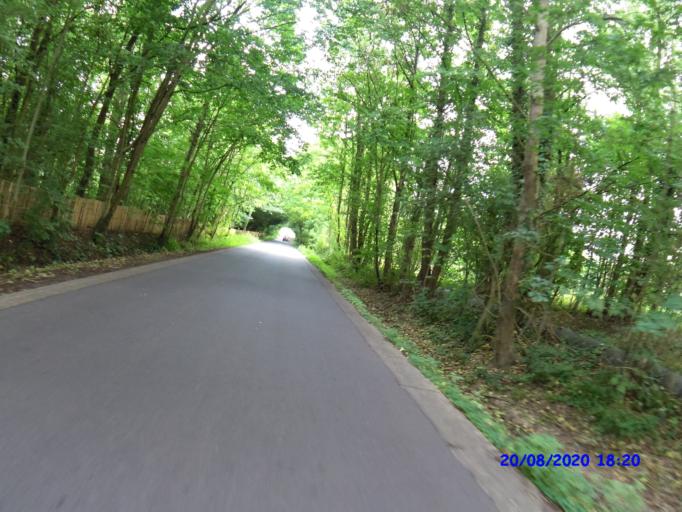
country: BE
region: Flanders
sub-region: Provincie Limburg
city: Nieuwerkerken
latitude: 50.8551
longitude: 5.2068
